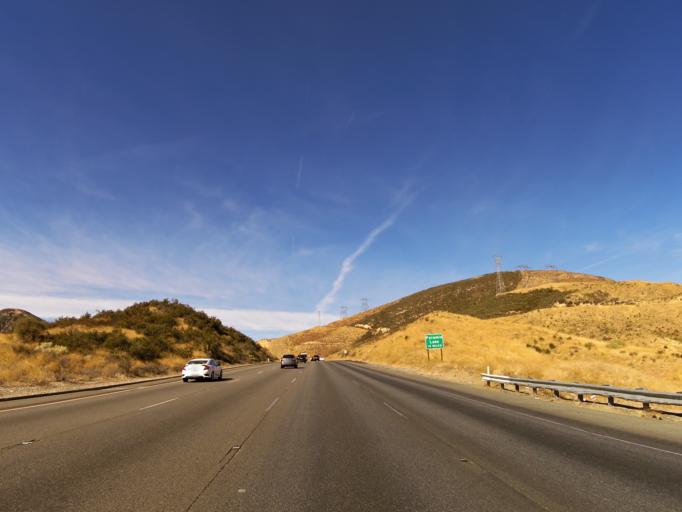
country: US
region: California
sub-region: Los Angeles County
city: Castaic
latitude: 34.5556
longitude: -118.6722
